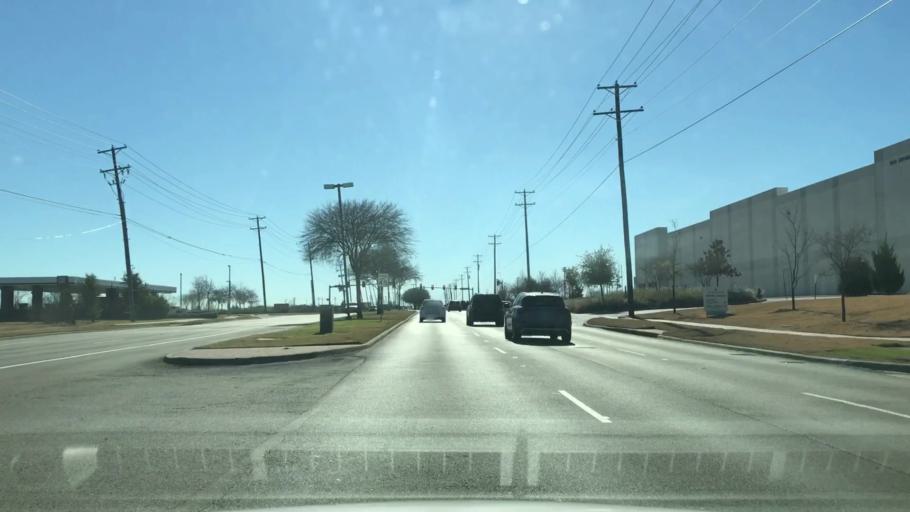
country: US
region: Texas
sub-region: Dallas County
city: Coppell
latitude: 32.9318
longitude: -96.9937
